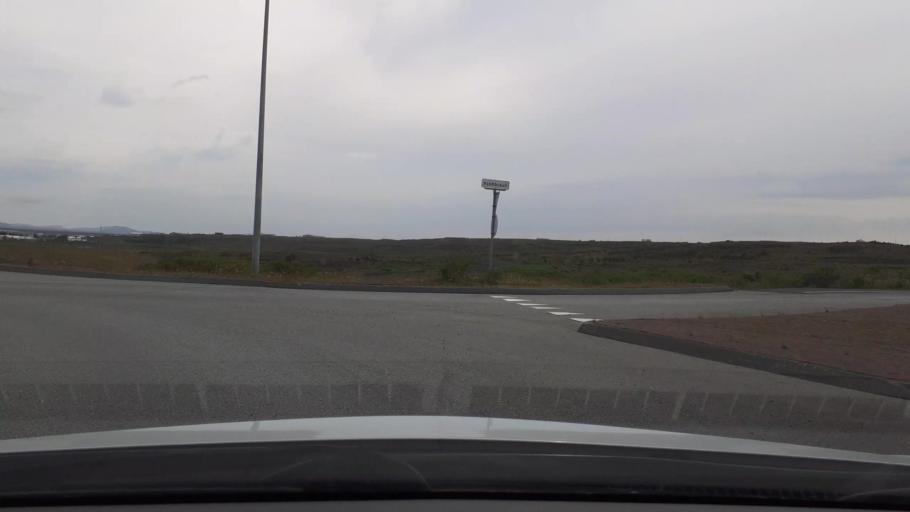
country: IS
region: Southern Peninsula
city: Reykjanesbaer
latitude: 63.9931
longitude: -22.5690
